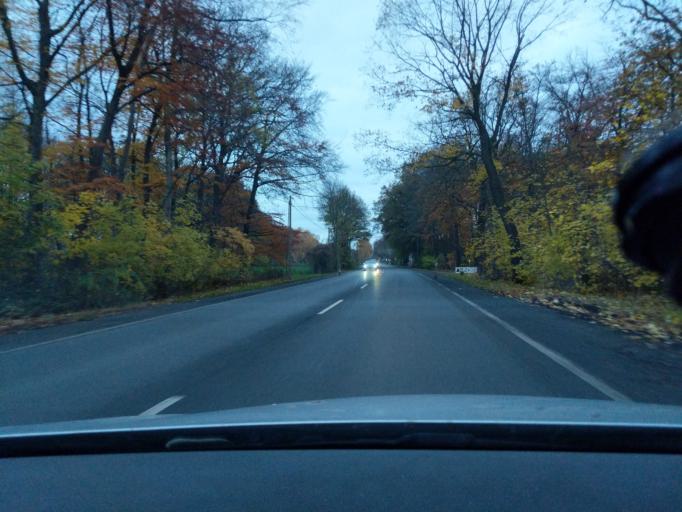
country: DE
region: North Rhine-Westphalia
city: Waltrop
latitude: 51.6373
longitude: 7.4364
